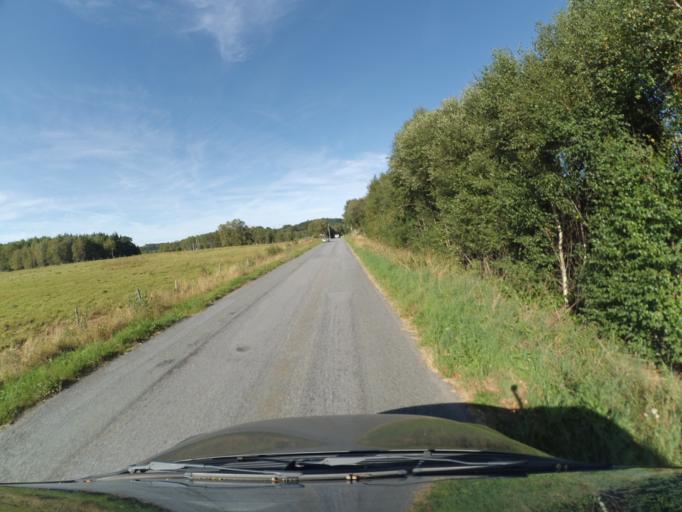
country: FR
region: Limousin
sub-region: Departement de la Correze
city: Bugeat
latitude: 45.7038
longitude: 2.0223
